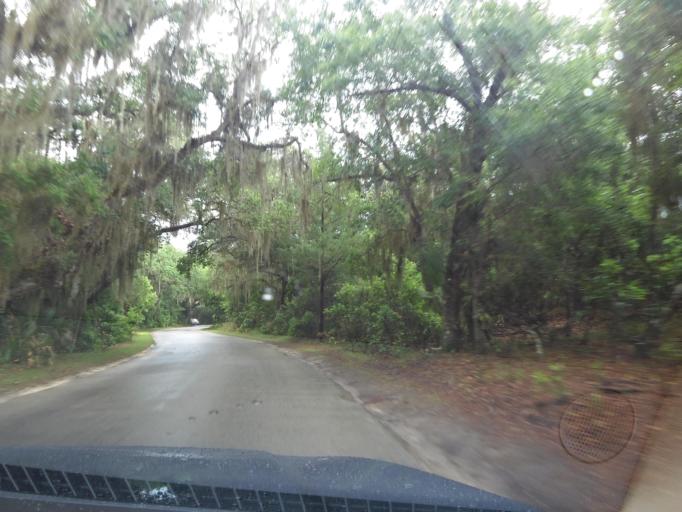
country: US
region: Florida
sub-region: Nassau County
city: Fernandina Beach
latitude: 30.7020
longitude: -81.4478
